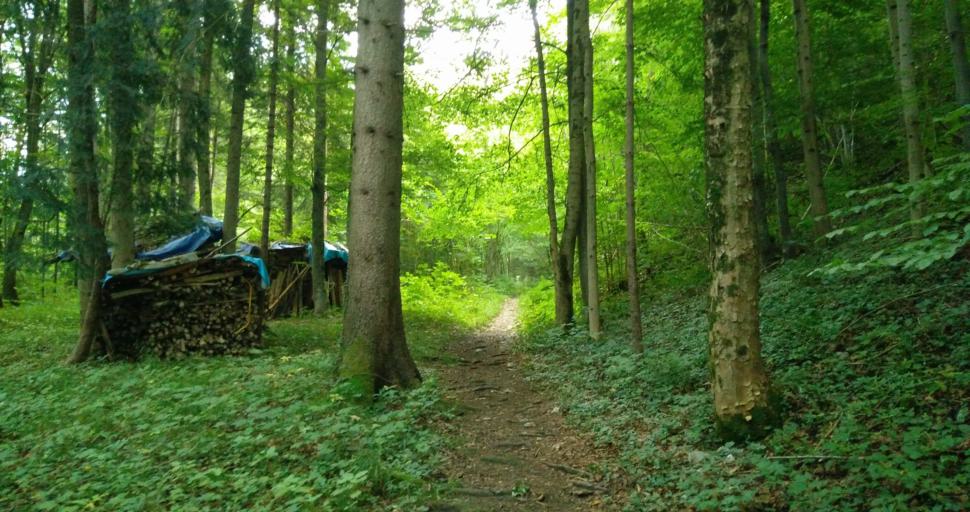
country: AT
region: Salzburg
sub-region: Politischer Bezirk Hallein
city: Adnet
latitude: 47.6571
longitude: 13.1431
